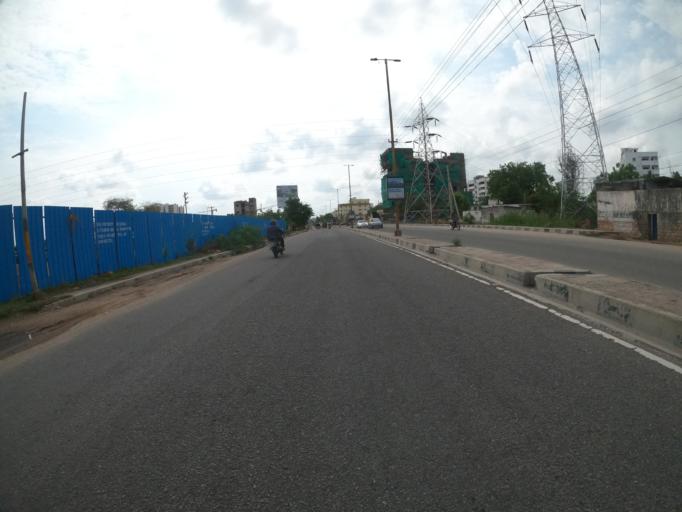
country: IN
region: Telangana
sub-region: Hyderabad
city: Hyderabad
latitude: 17.3825
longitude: 78.3648
